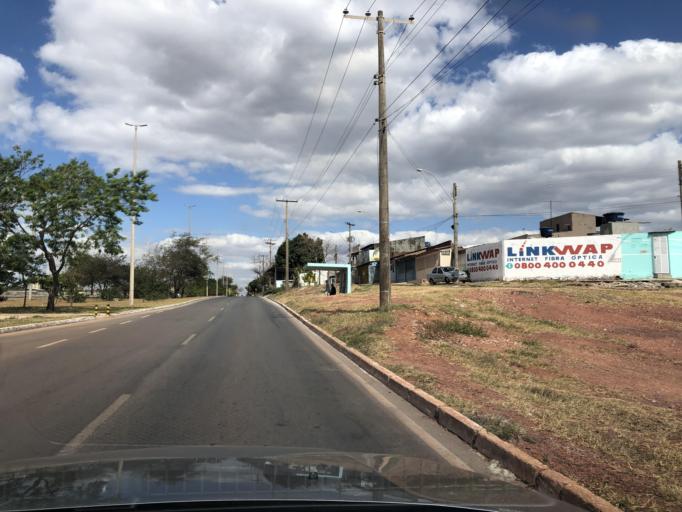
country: BR
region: Federal District
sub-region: Brasilia
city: Brasilia
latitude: -15.8897
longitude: -48.1407
